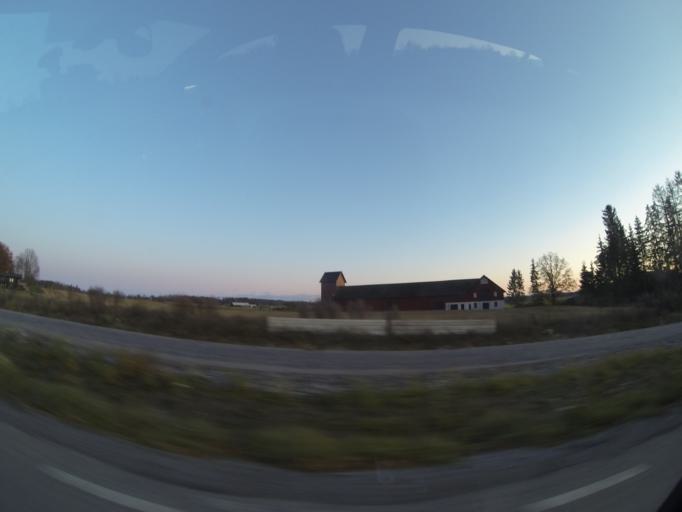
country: SE
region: OErebro
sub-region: Lindesbergs Kommun
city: Frovi
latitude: 59.3136
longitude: 15.3722
